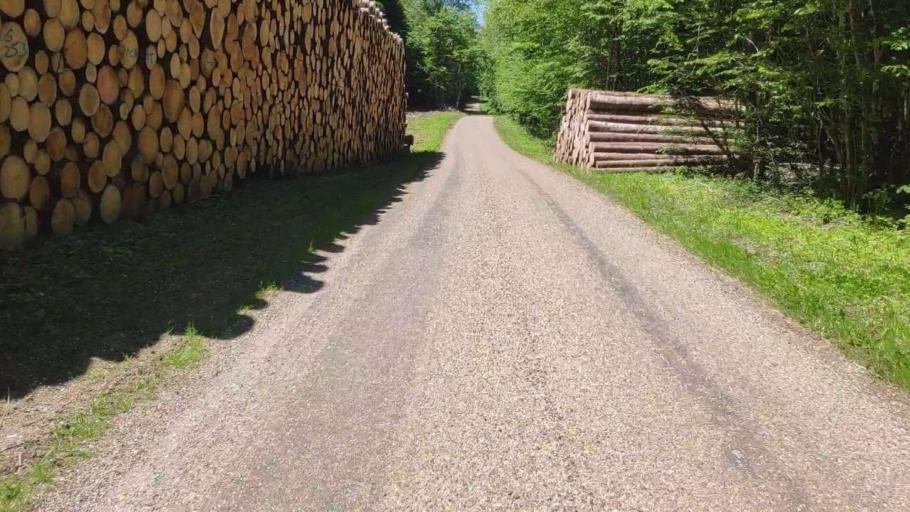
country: FR
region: Franche-Comte
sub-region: Departement du Jura
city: Poligny
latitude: 46.7349
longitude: 5.6703
